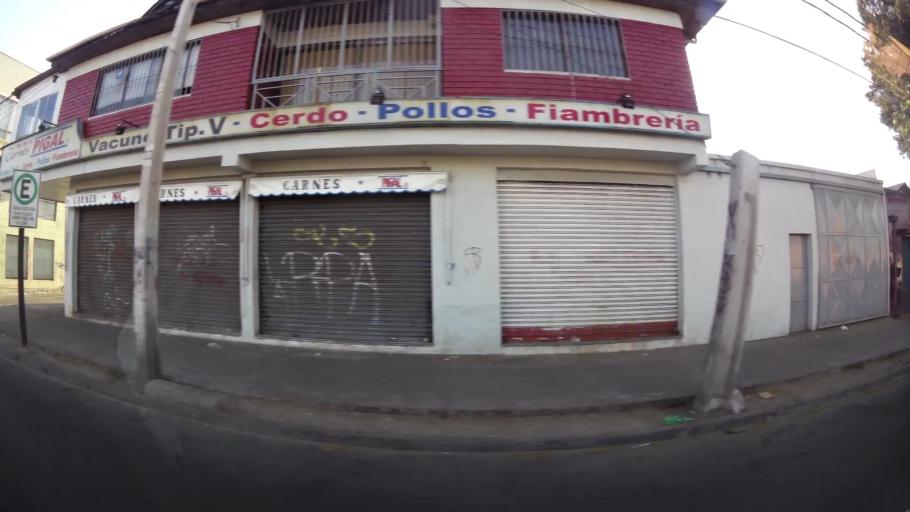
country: CL
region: Santiago Metropolitan
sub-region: Provincia de Santiago
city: Lo Prado
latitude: -33.4430
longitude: -70.7233
